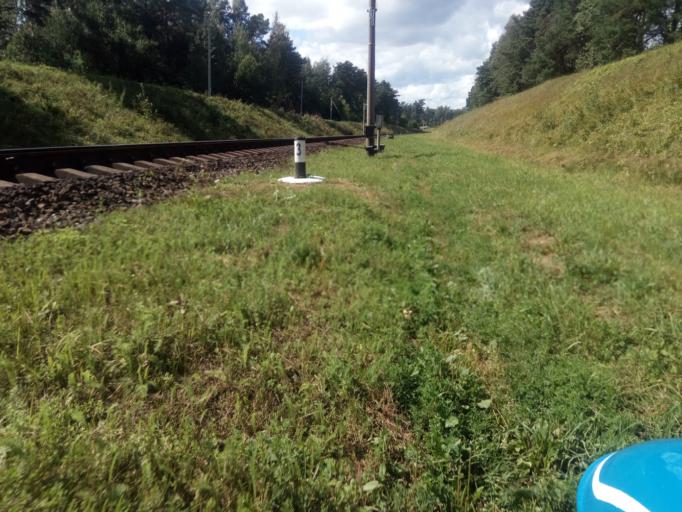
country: BY
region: Vitebsk
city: Dzisna
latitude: 55.6788
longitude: 28.2950
